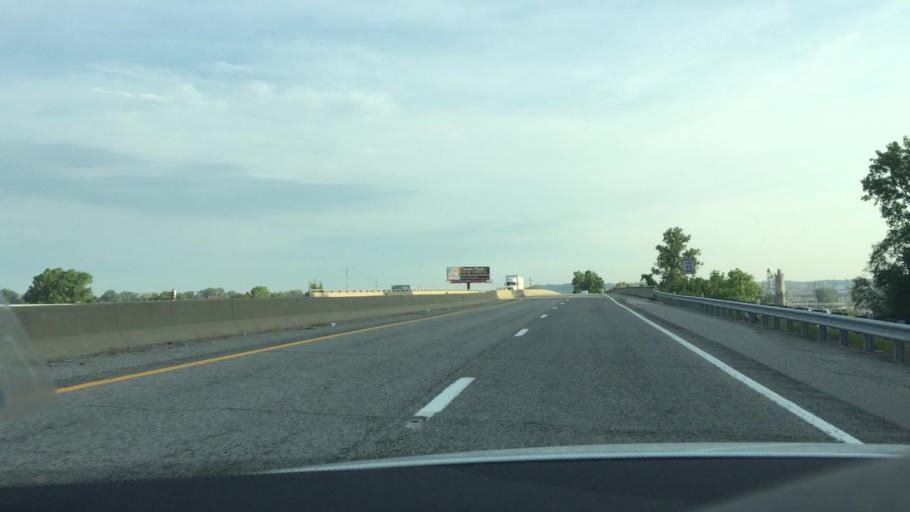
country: US
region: Kansas
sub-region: Doniphan County
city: Elwood
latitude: 39.7369
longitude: -94.8506
